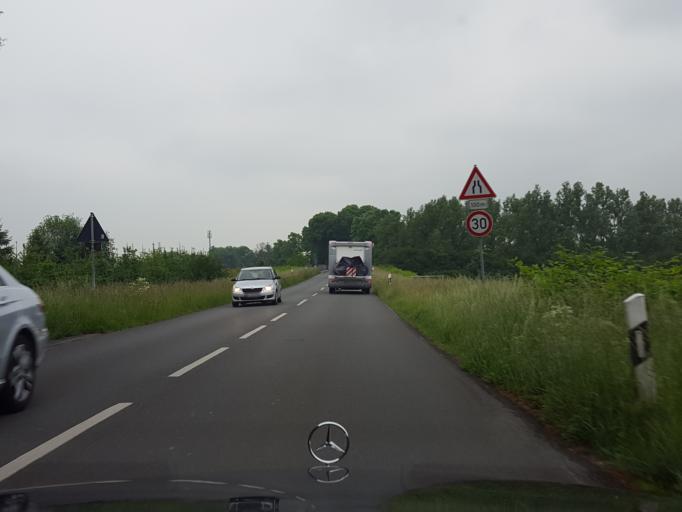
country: DE
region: North Rhine-Westphalia
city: Olfen
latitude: 51.7040
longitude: 7.3130
